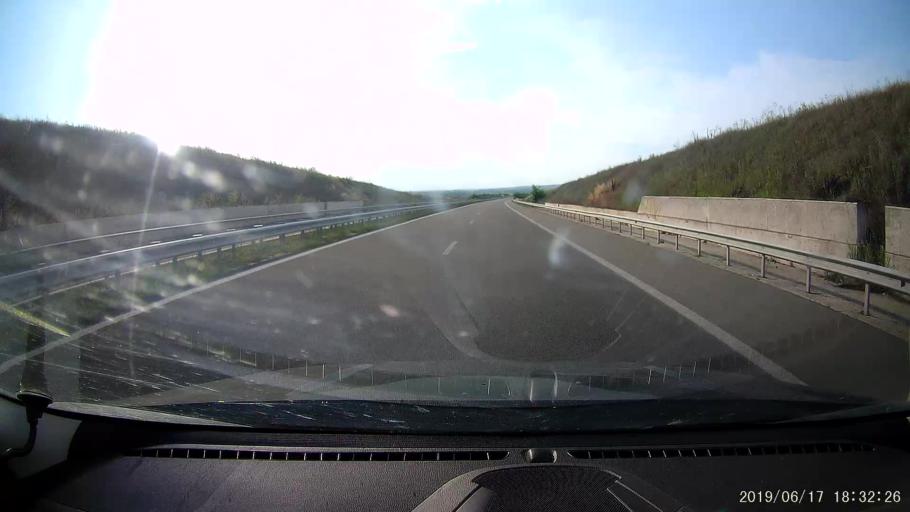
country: BG
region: Khaskovo
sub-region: Obshtina Dimitrovgrad
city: Dimitrovgrad
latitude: 42.0598
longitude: 25.4787
